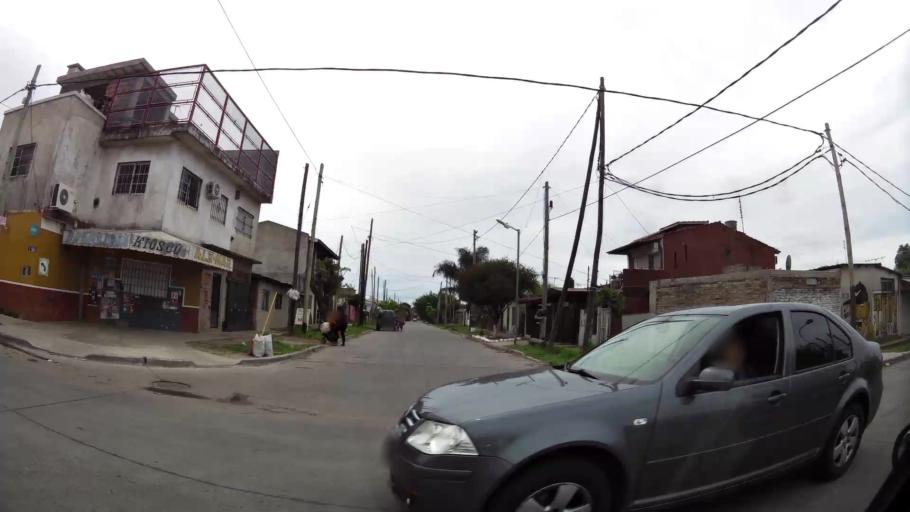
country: AR
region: Buenos Aires
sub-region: Partido de Quilmes
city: Quilmes
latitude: -34.7544
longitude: -58.2632
